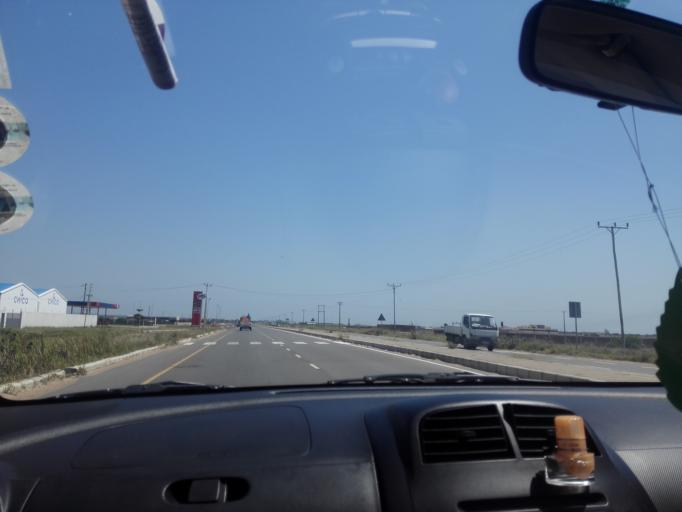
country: MZ
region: Maputo City
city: Maputo
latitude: -25.8438
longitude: 32.6718
